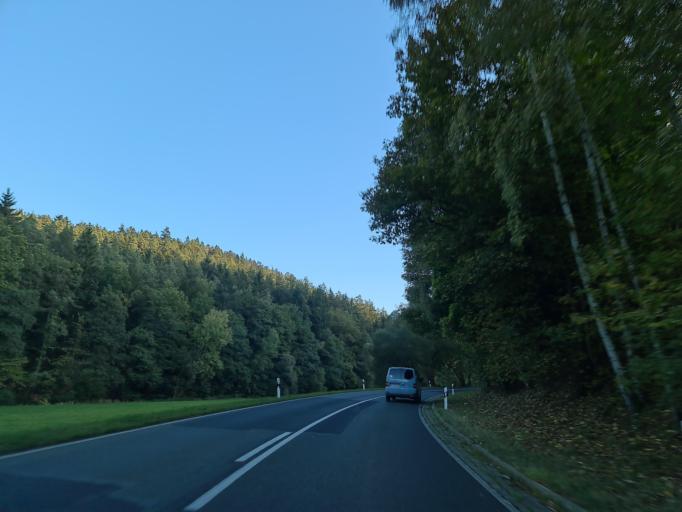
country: DE
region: Saxony
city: Elsterberg
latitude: 50.5975
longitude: 12.1403
